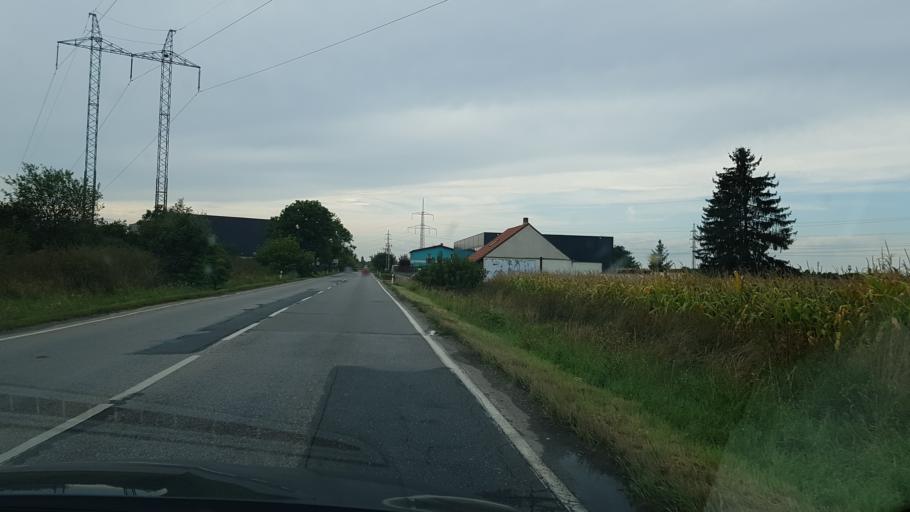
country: CZ
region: Central Bohemia
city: Sestajovice
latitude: 50.1239
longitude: 14.6807
